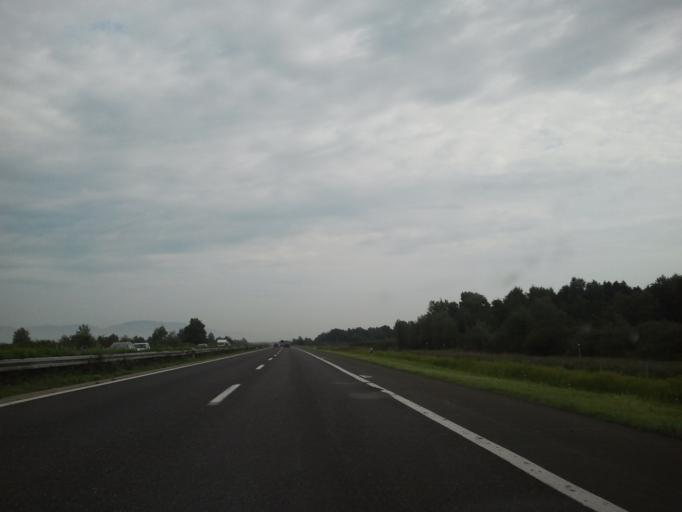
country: HR
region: Zagrebacka
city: Jastrebarsko
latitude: 45.5803
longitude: 15.6239
